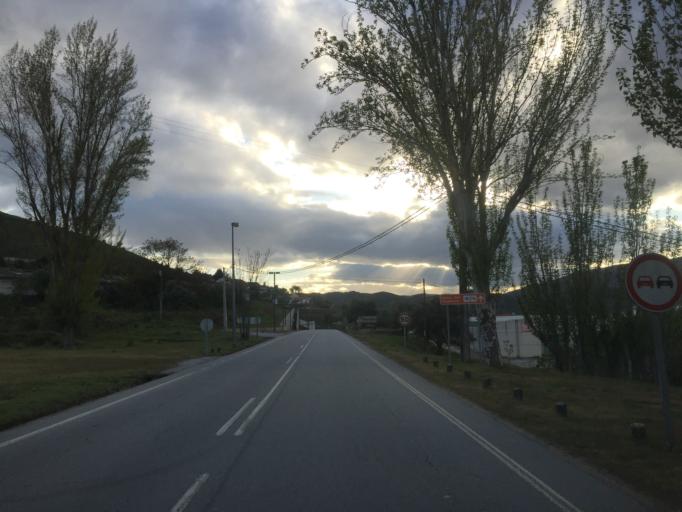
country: PT
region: Braganca
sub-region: Torre de Moncorvo
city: Torre de Moncorvo
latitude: 41.1320
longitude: -7.1153
